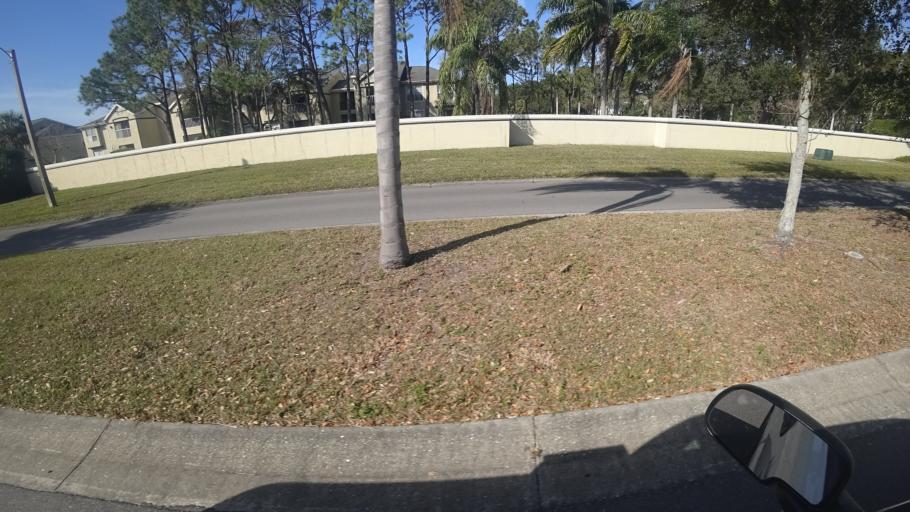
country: US
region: Florida
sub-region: Manatee County
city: South Bradenton
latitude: 27.4574
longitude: -82.6082
